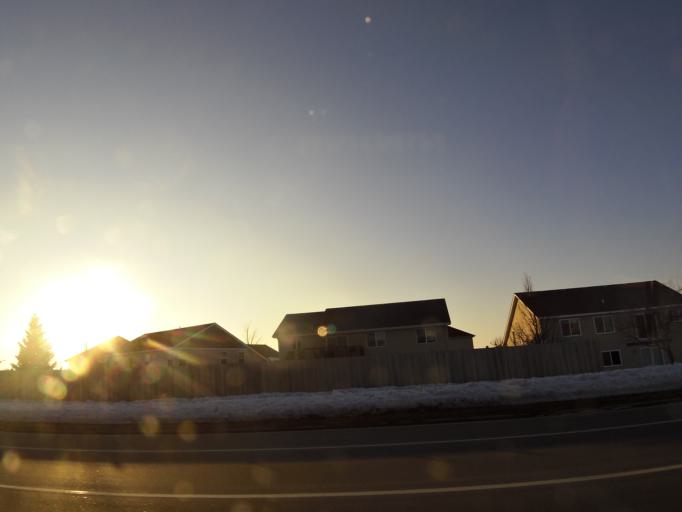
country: US
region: Minnesota
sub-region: Scott County
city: Shakopee
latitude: 44.7727
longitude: -93.5202
